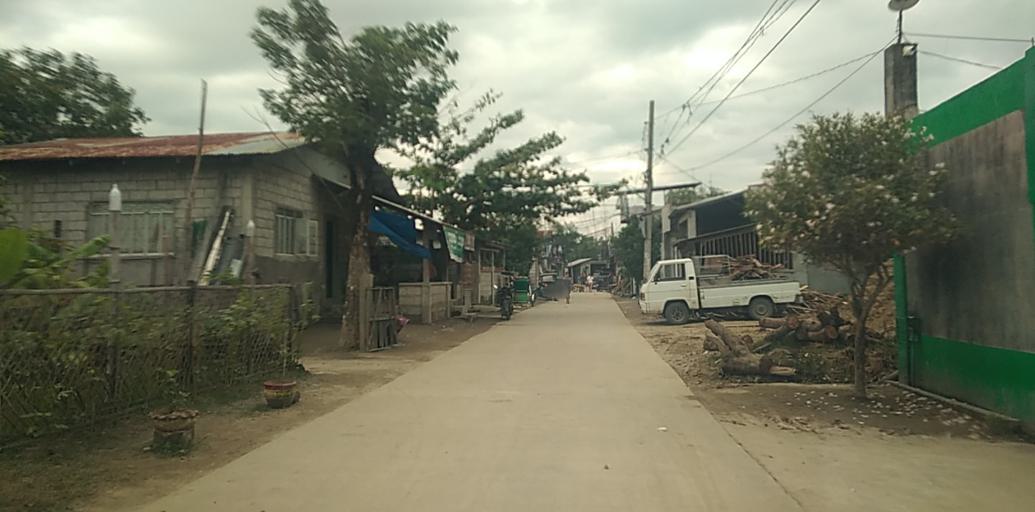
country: PH
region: Central Luzon
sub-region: Province of Pampanga
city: San Fernando
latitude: 15.0035
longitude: 120.7009
